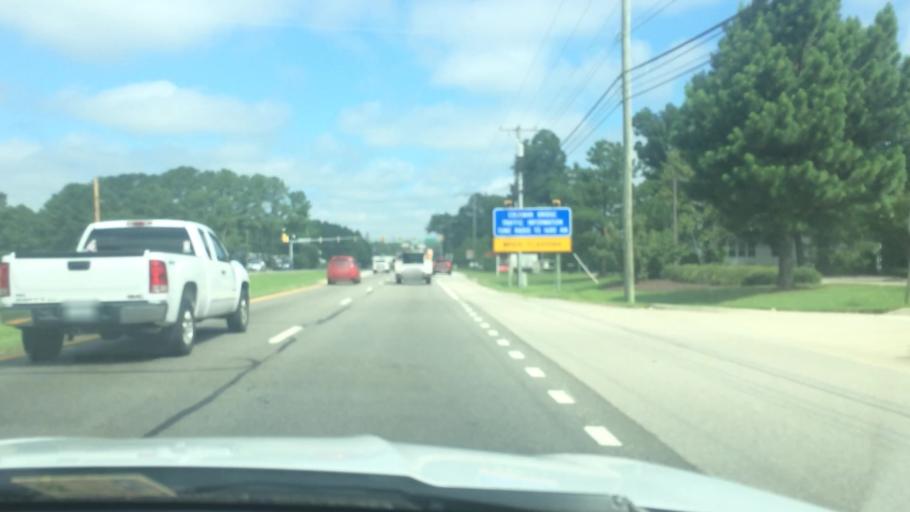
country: US
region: Virginia
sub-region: York County
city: Yorktown
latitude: 37.1765
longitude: -76.4777
